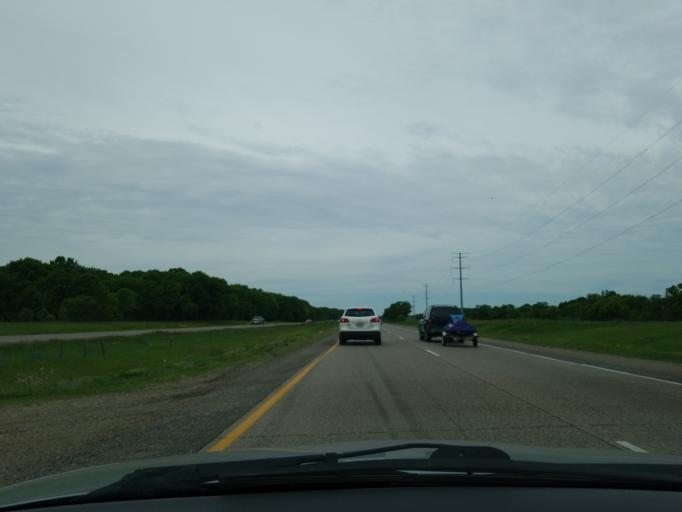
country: US
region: Minnesota
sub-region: Wright County
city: Monticello
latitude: 45.3303
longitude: -93.8556
